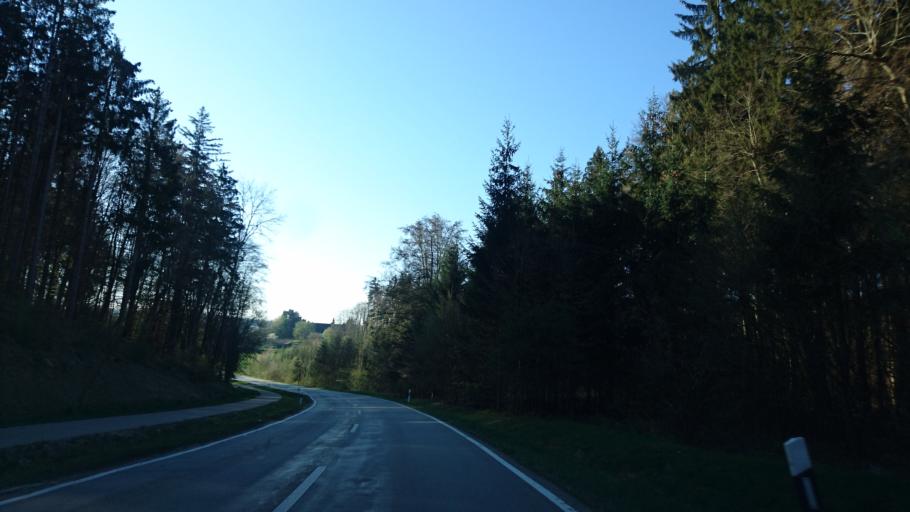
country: DE
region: Bavaria
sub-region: Swabia
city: Aystetten
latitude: 48.4455
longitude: 10.7764
